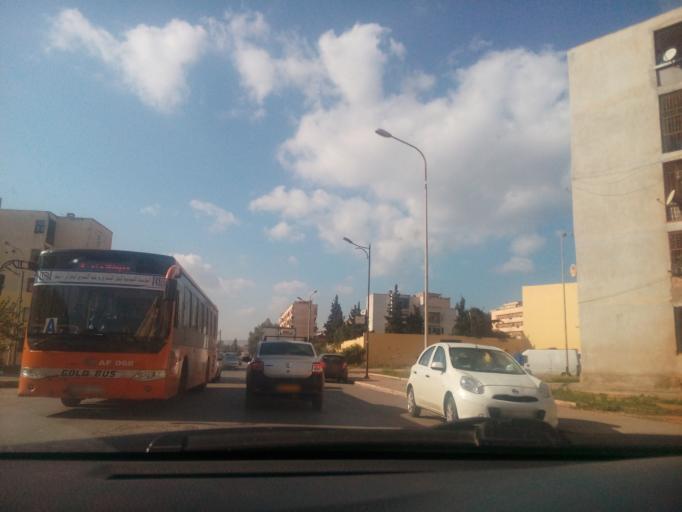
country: DZ
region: Oran
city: Oran
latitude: 35.7037
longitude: -0.6008
